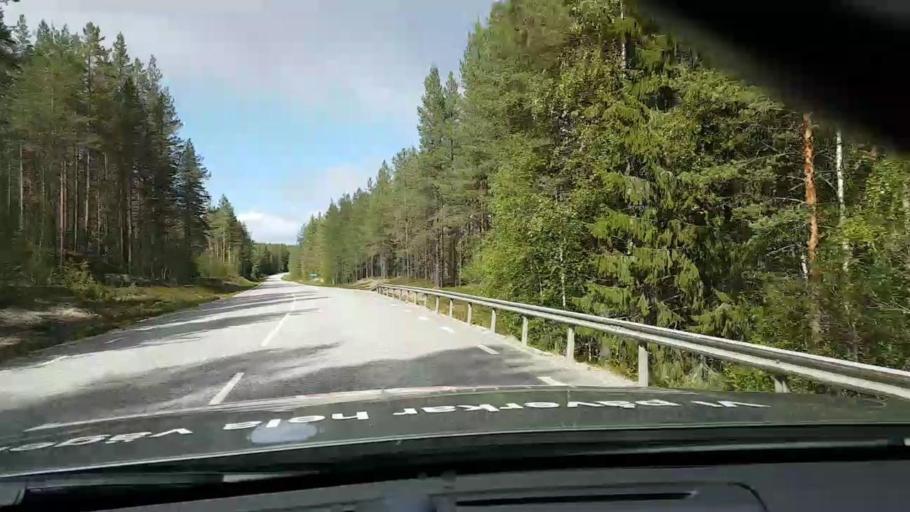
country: SE
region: Vaesternorrland
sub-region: OErnskoeldsviks Kommun
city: Bredbyn
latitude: 63.6906
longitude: 17.7701
